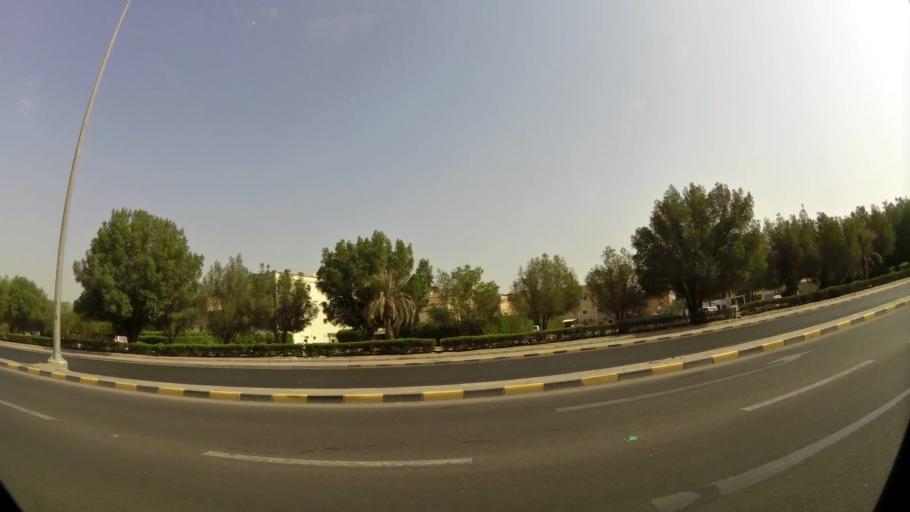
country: KW
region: Al Asimah
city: Ar Rabiyah
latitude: 29.2850
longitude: 47.8842
